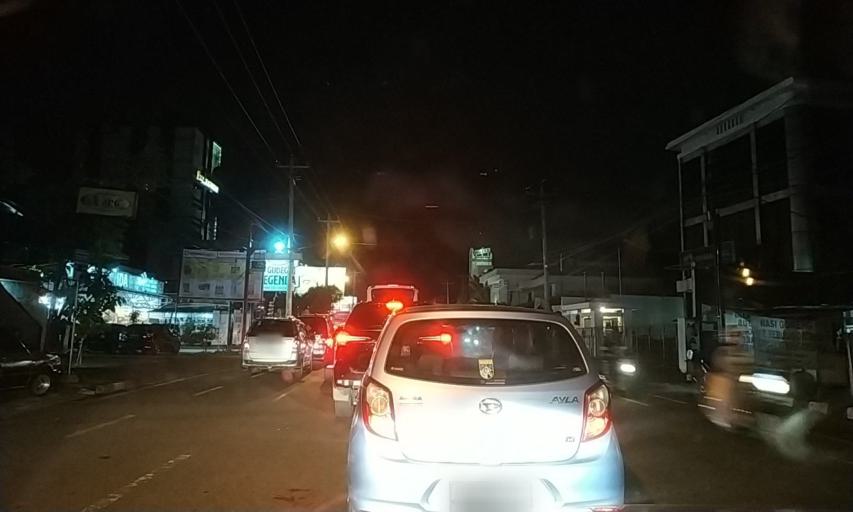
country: ID
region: Daerah Istimewa Yogyakarta
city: Yogyakarta
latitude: -7.7923
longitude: 110.3535
